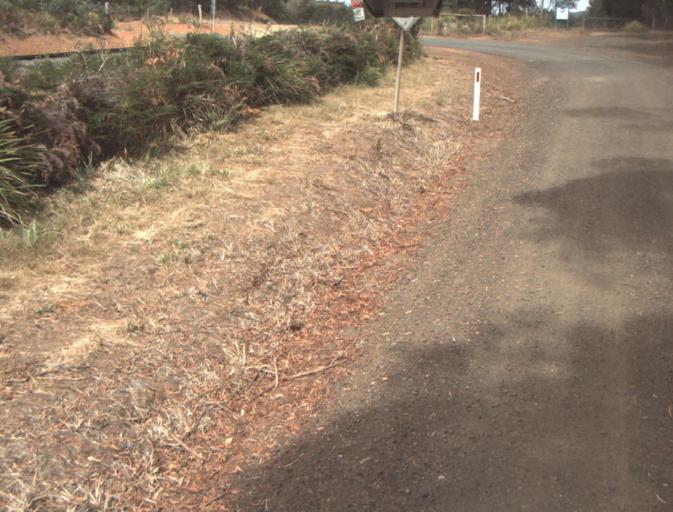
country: AU
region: Tasmania
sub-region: Launceston
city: Mayfield
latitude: -41.2786
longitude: 147.0528
